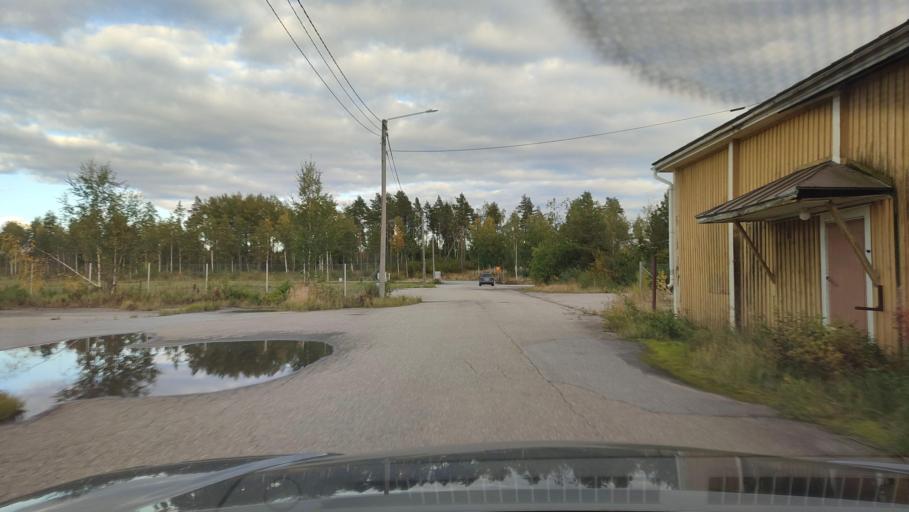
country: FI
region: Ostrobothnia
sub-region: Sydosterbotten
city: Kristinestad
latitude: 62.2647
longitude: 21.3816
